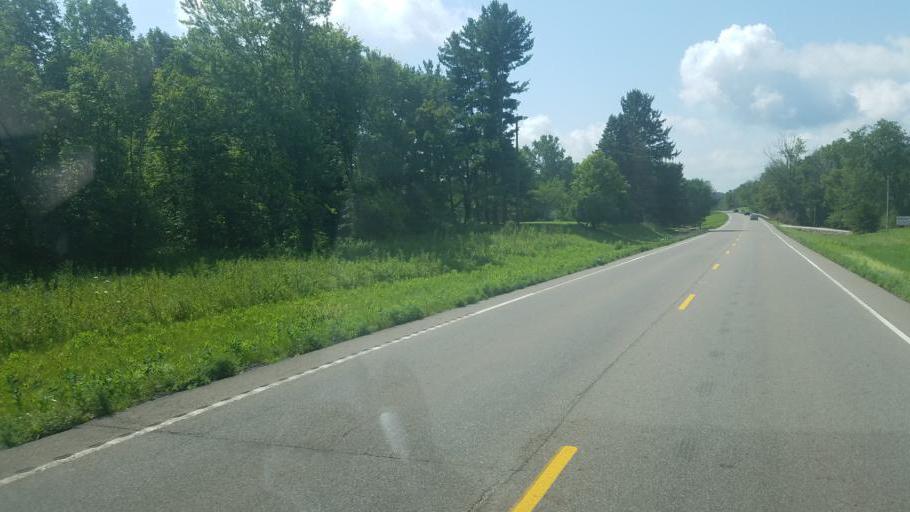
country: US
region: Ohio
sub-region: Licking County
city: Hebron
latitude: 39.9872
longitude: -82.5254
